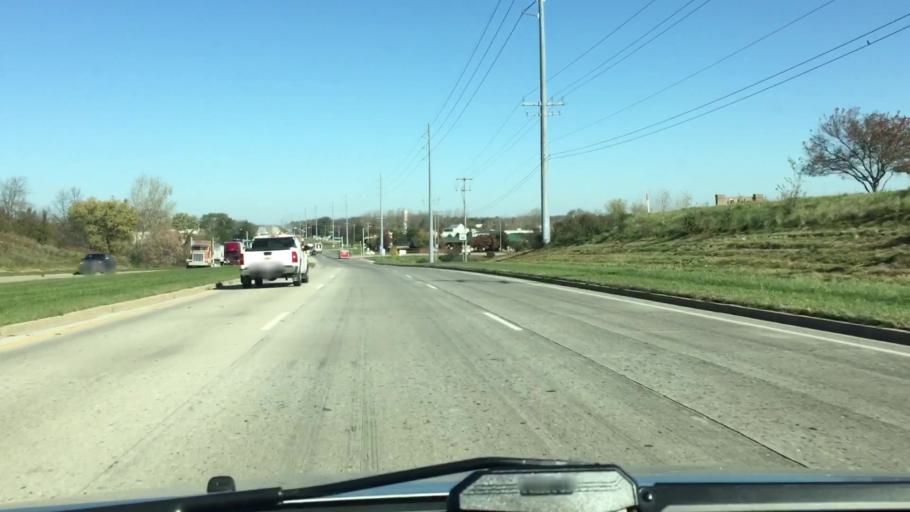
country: US
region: Wisconsin
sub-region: Waukesha County
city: Waukesha
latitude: 43.0558
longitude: -88.2058
